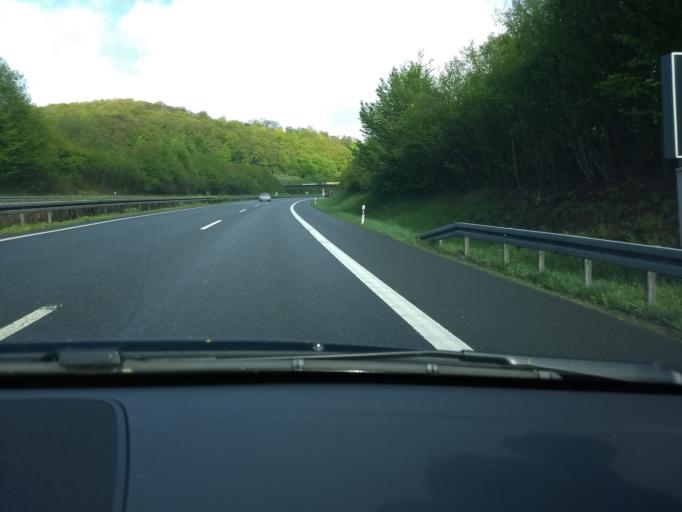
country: DE
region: North Rhine-Westphalia
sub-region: Regierungsbezirk Arnsberg
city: Arnsberg
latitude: 51.3603
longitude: 8.1655
